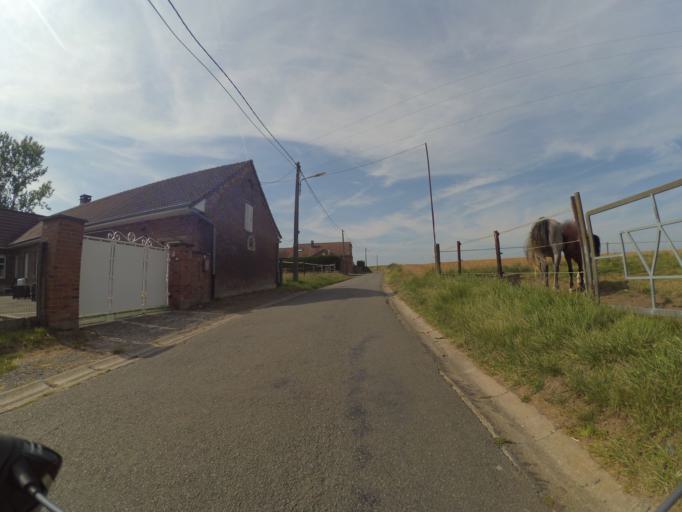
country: BE
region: Wallonia
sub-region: Province du Hainaut
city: Flobecq
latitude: 50.7234
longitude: 3.7329
